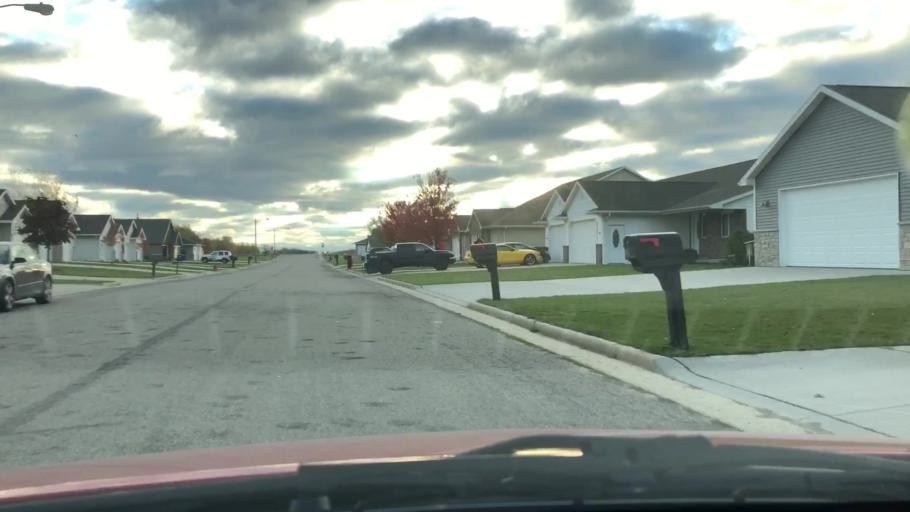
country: US
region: Wisconsin
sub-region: Outagamie County
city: Seymour
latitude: 44.5096
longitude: -88.3133
